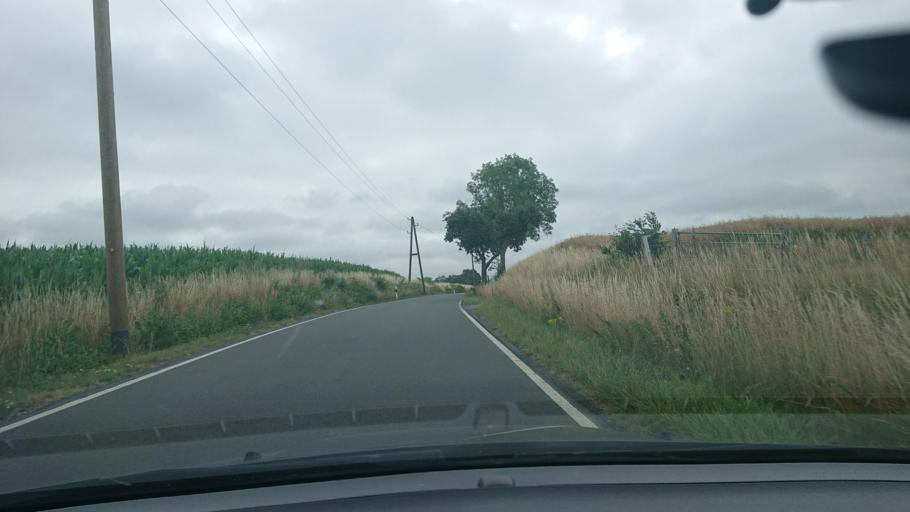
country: DE
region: North Rhine-Westphalia
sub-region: Regierungsbezirk Arnsberg
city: Soest
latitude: 51.5360
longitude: 8.0699
